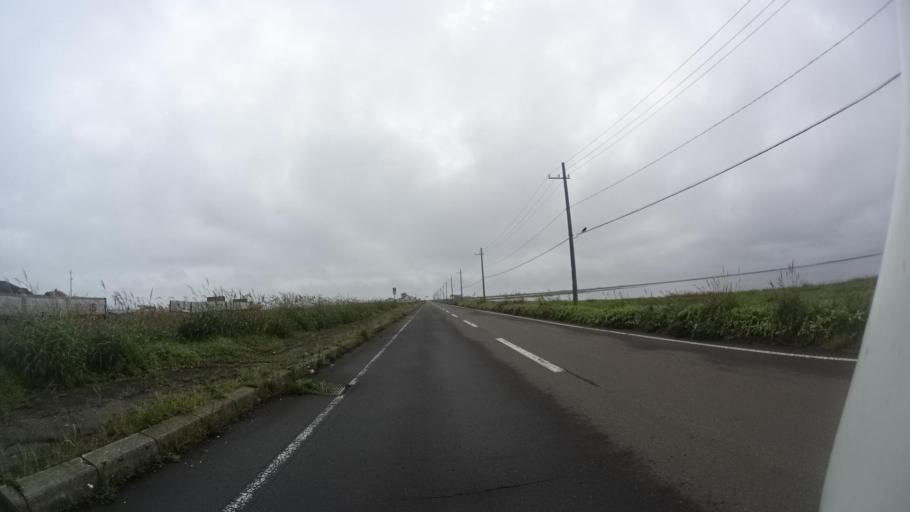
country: JP
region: Hokkaido
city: Shibetsu
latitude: 43.5956
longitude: 145.3252
